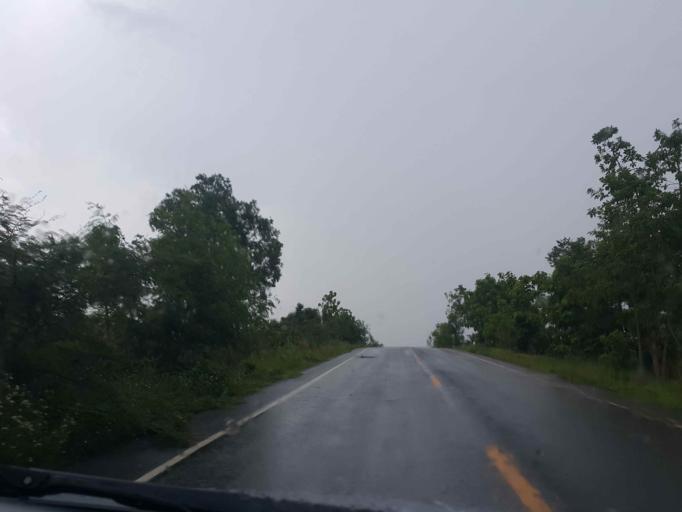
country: TH
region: Phayao
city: Dok Kham Tai
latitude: 19.0288
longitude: 99.9673
